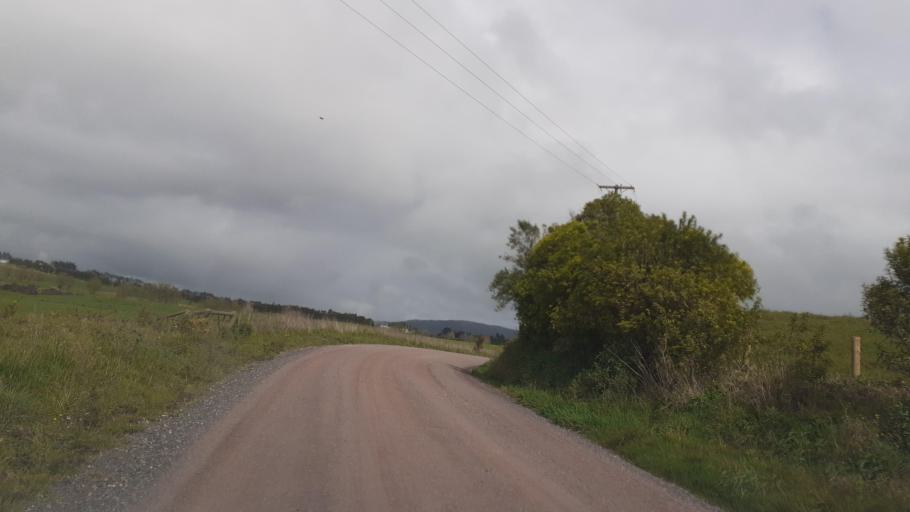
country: NZ
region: Northland
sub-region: Far North District
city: Waimate North
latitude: -35.2434
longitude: 173.8103
